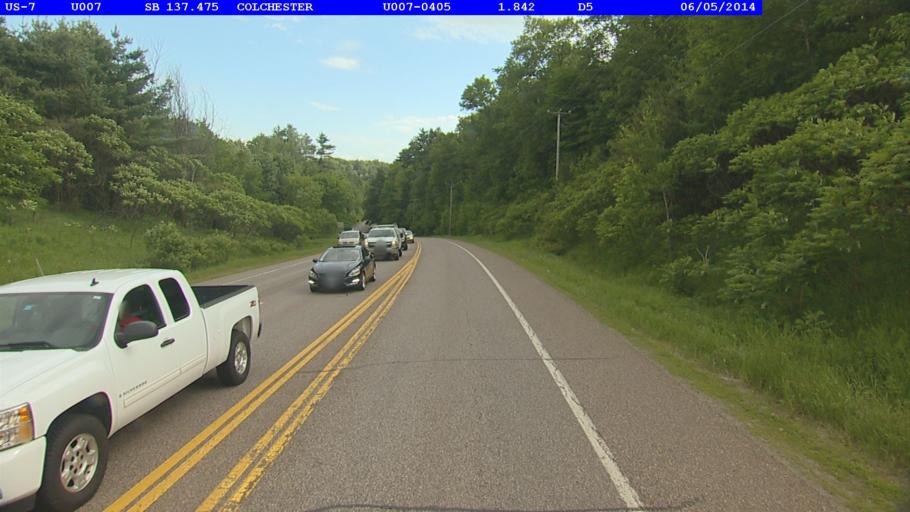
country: US
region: Vermont
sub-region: Chittenden County
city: Colchester
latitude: 44.5267
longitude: -73.1729
